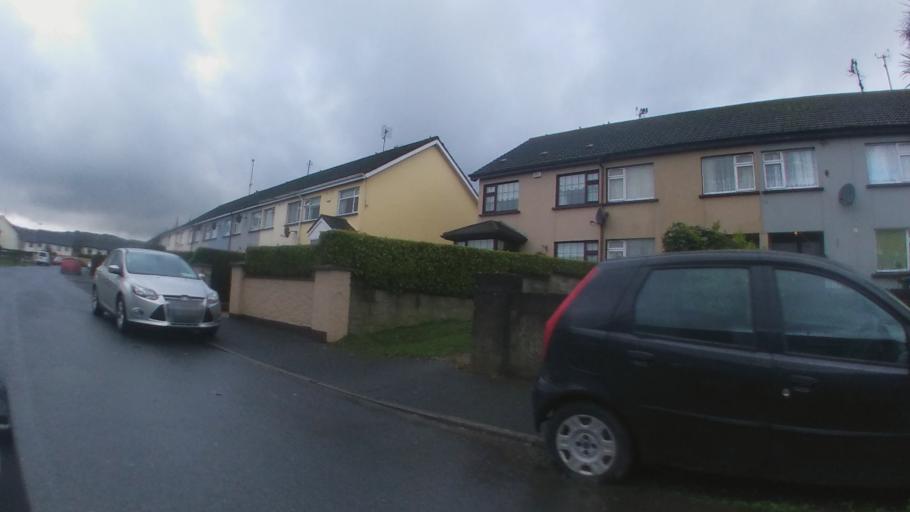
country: IE
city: Newtownmountkennedy
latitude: 53.0869
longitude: -6.1122
